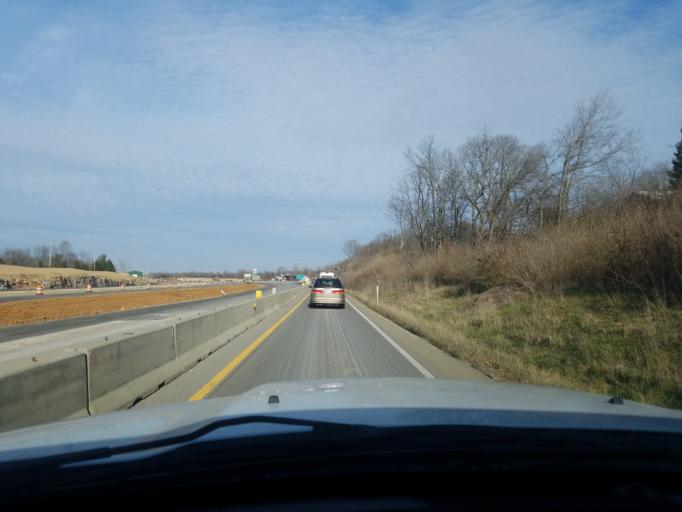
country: US
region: Indiana
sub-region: Monroe County
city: Bloomington
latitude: 39.2582
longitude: -86.5246
